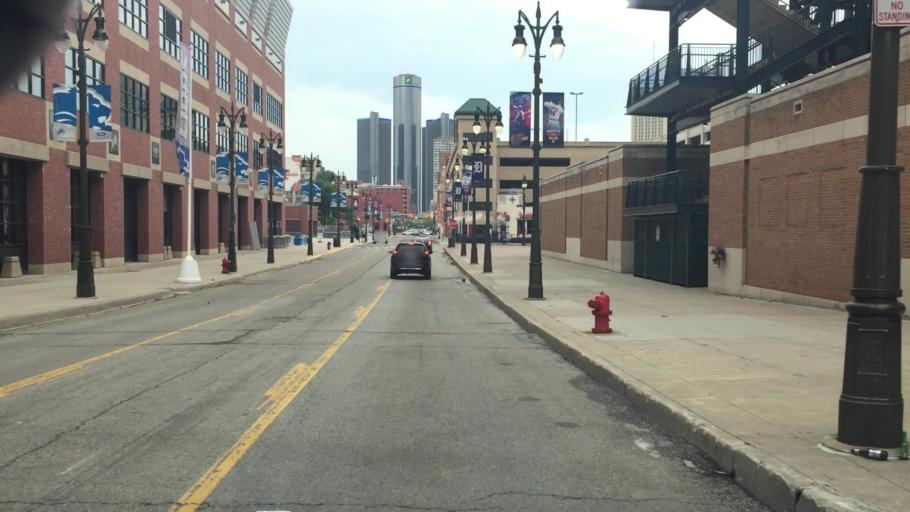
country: US
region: Michigan
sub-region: Wayne County
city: Detroit
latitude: 42.3397
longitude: -83.0473
